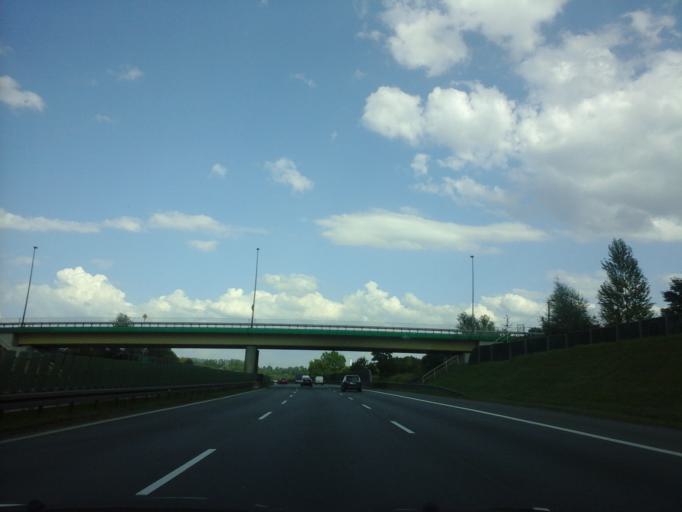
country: PL
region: Lesser Poland Voivodeship
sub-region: Powiat krakowski
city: Wrzasowice
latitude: 50.0003
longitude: 19.9566
